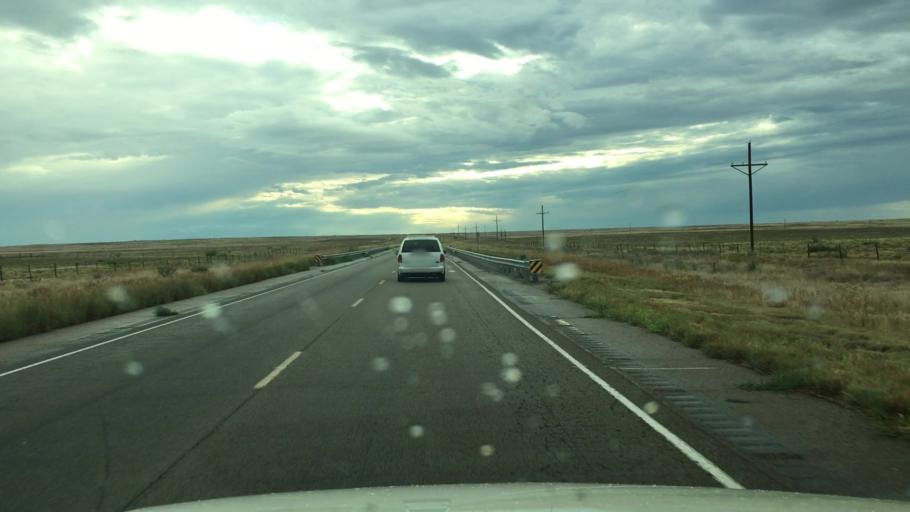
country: US
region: New Mexico
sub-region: Chaves County
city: Dexter
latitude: 33.4061
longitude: -104.3035
